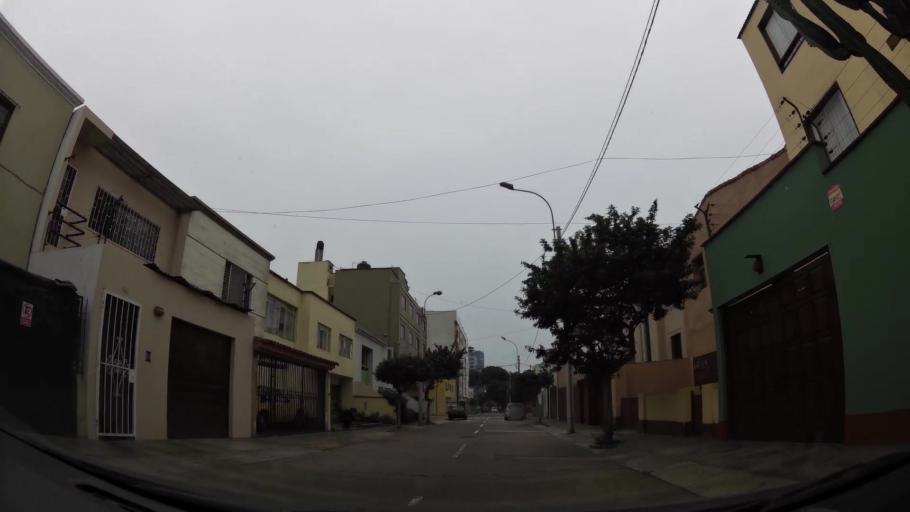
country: PE
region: Lima
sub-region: Lima
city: San Isidro
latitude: -12.1165
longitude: -77.0401
